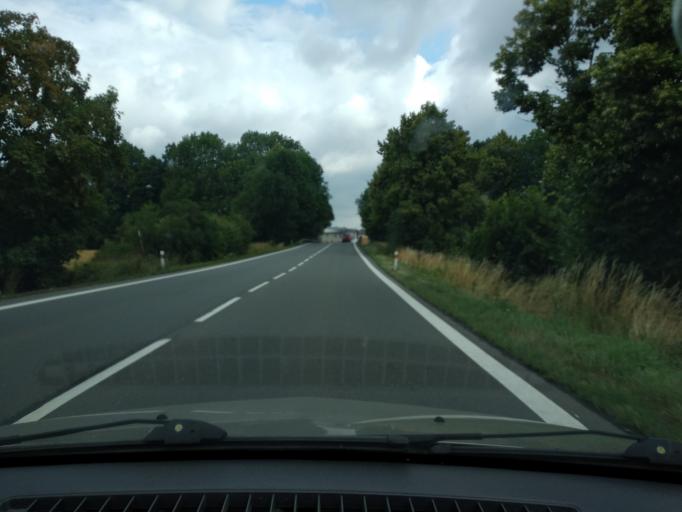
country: CZ
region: Olomoucky
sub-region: Okres Sumperk
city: Bludov
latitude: 49.9260
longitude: 16.9190
